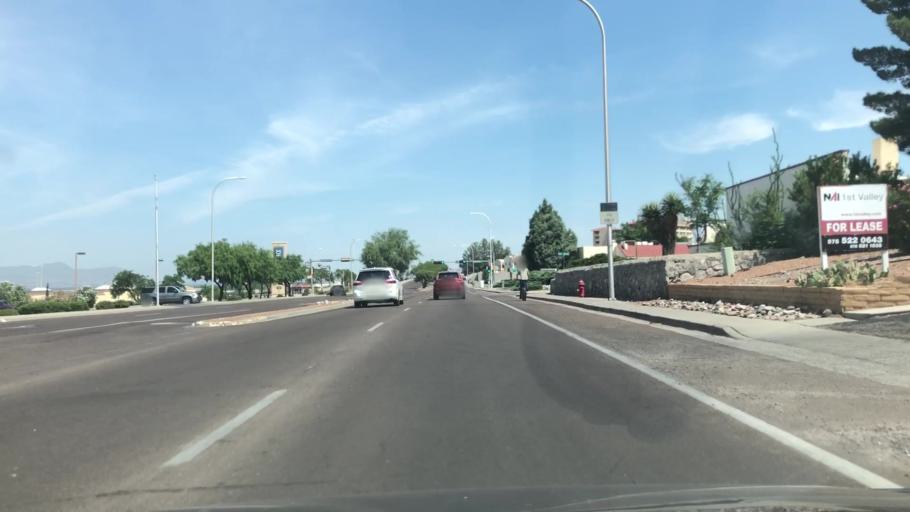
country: US
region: New Mexico
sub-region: Dona Ana County
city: University Park
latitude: 32.3087
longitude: -106.7396
